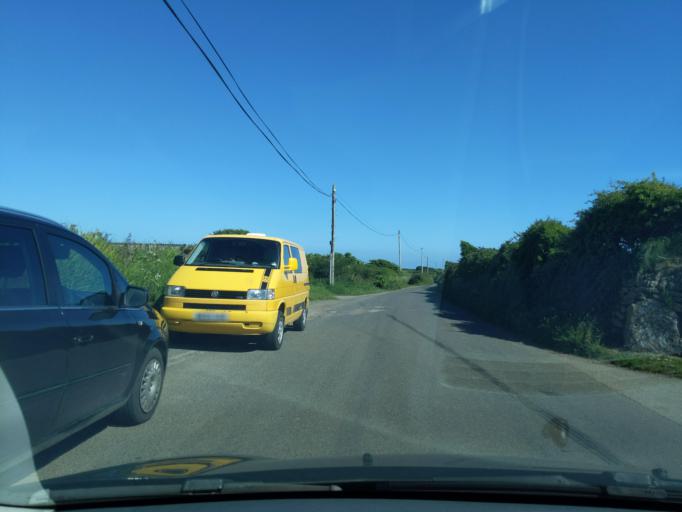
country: GB
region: England
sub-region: Cornwall
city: St. Buryan
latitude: 50.0665
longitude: -5.6043
